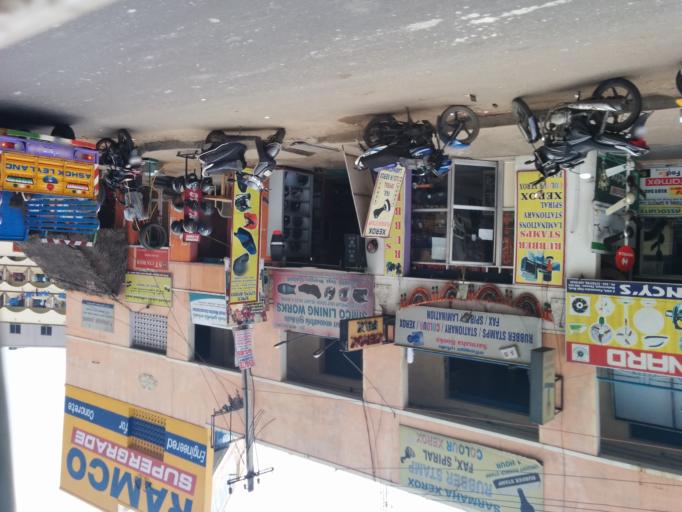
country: IN
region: Tamil Nadu
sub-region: Thiruvallur
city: Porur
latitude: 13.0656
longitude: 80.1736
